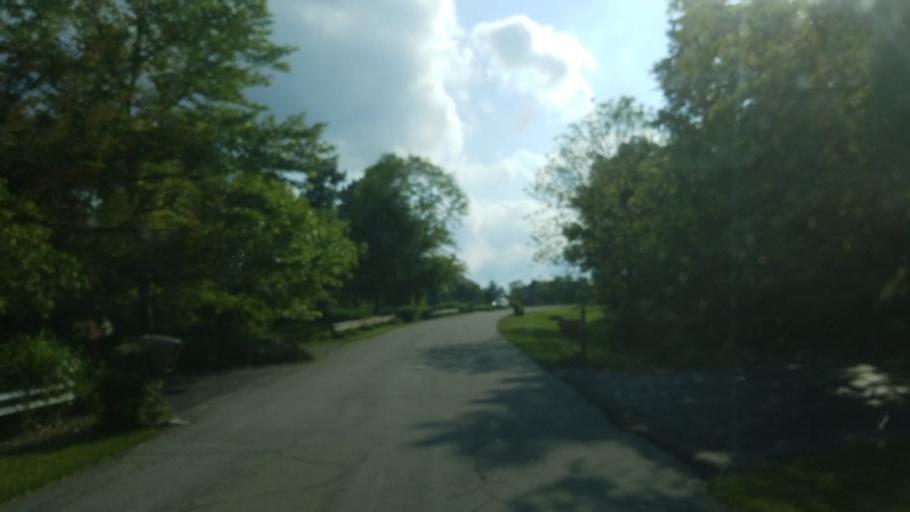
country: US
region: Ohio
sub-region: Delaware County
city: Sunbury
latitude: 40.1844
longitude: -82.8624
